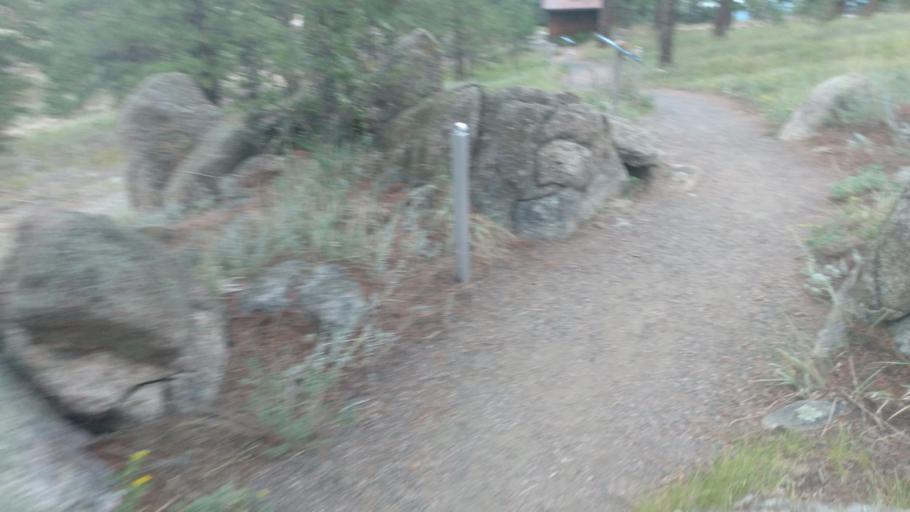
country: US
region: Colorado
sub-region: Boulder County
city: Boulder
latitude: 40.0039
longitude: -105.3061
